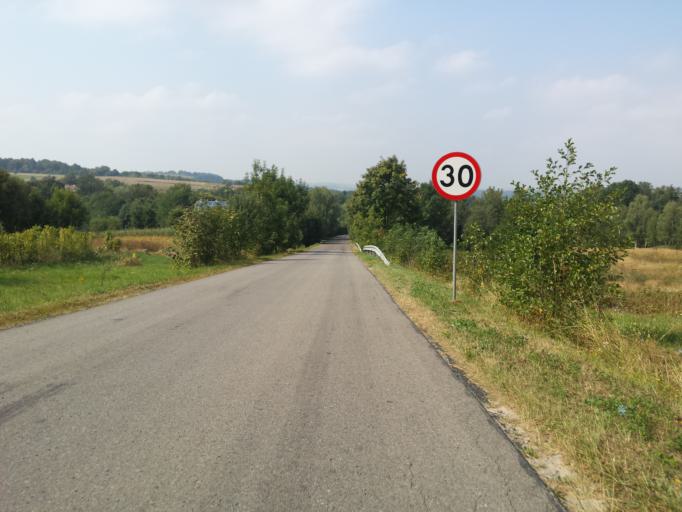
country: PL
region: Subcarpathian Voivodeship
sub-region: Powiat rzeszowski
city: Blazowa
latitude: 49.8441
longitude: 22.1440
